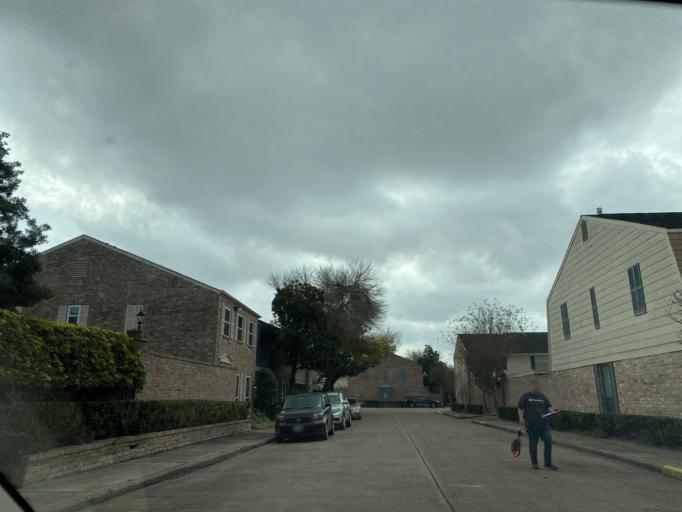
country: US
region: Texas
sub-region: Harris County
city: Piney Point Village
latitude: 29.7428
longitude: -95.4990
